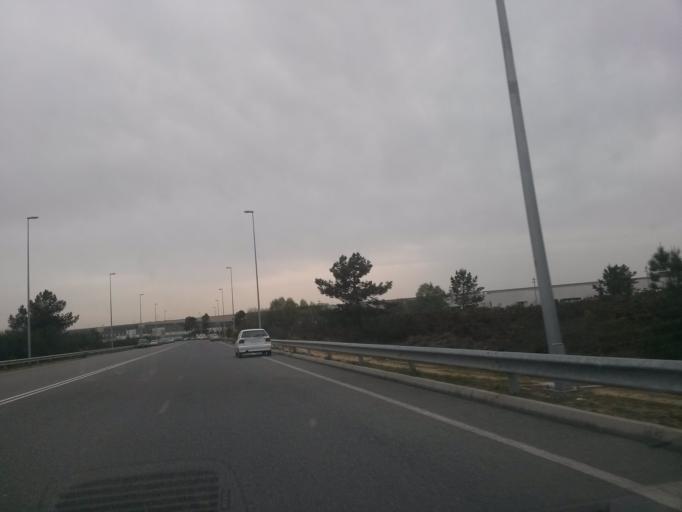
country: ES
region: Galicia
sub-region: Provincia de Lugo
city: Lugo
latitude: 43.0204
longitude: -7.5277
